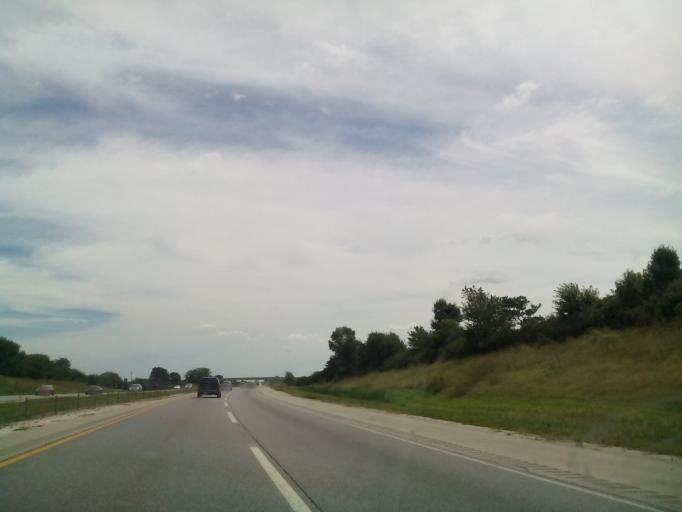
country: US
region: Illinois
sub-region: Kane County
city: Maple Park
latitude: 41.8987
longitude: -88.6451
